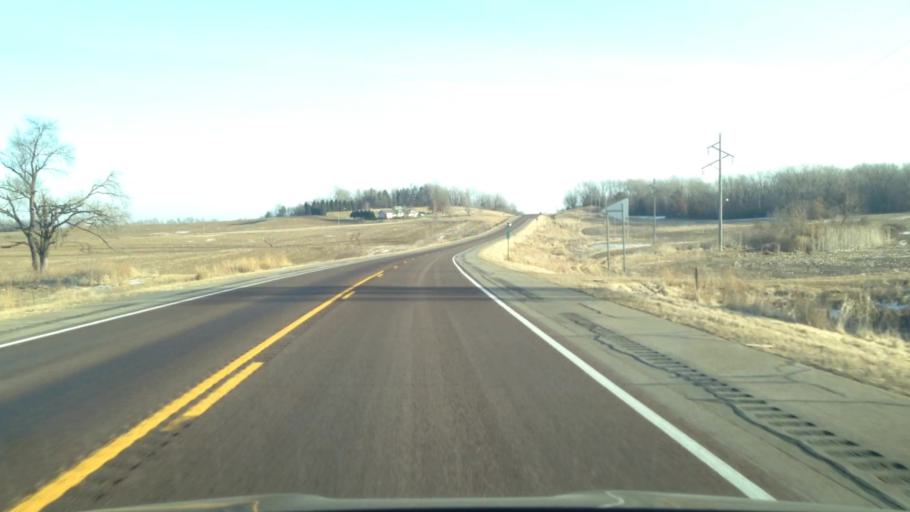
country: US
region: Minnesota
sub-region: Goodhue County
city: Goodhue
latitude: 44.4372
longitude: -92.6119
